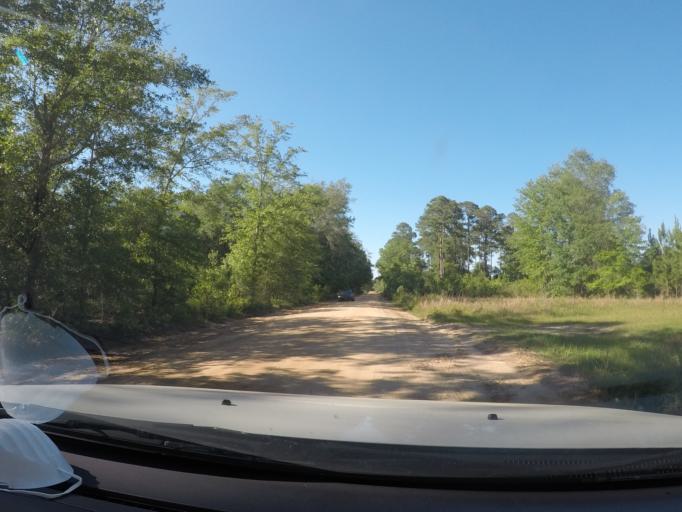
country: US
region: Georgia
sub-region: Bulloch County
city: Brooklet
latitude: 32.3106
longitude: -81.7461
